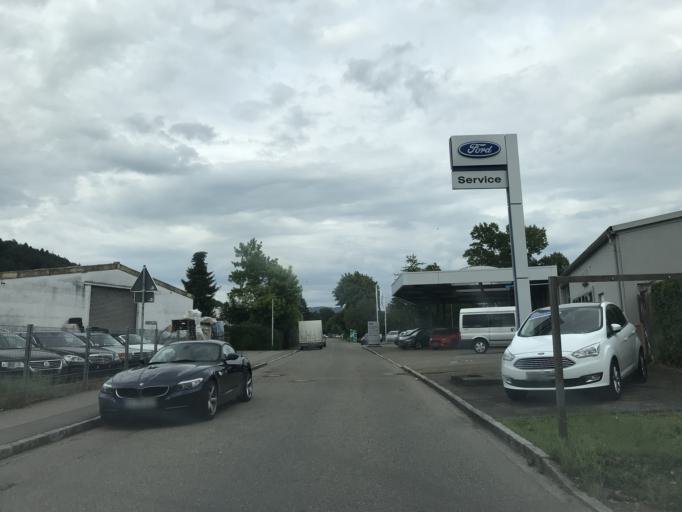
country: DE
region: Baden-Wuerttemberg
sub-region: Freiburg Region
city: Schopfheim
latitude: 47.6460
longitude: 7.8034
